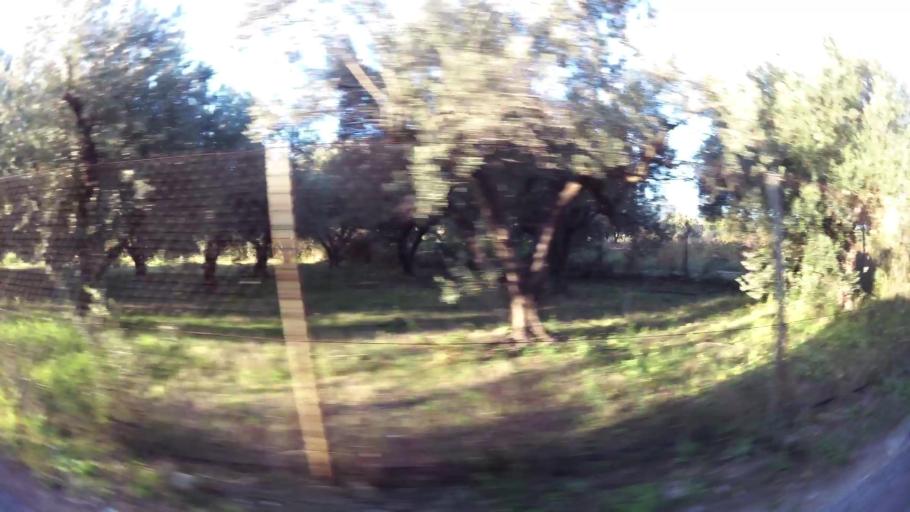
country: GR
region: Attica
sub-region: Nomarchia Anatolikis Attikis
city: Pallini
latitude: 37.9965
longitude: 23.8875
